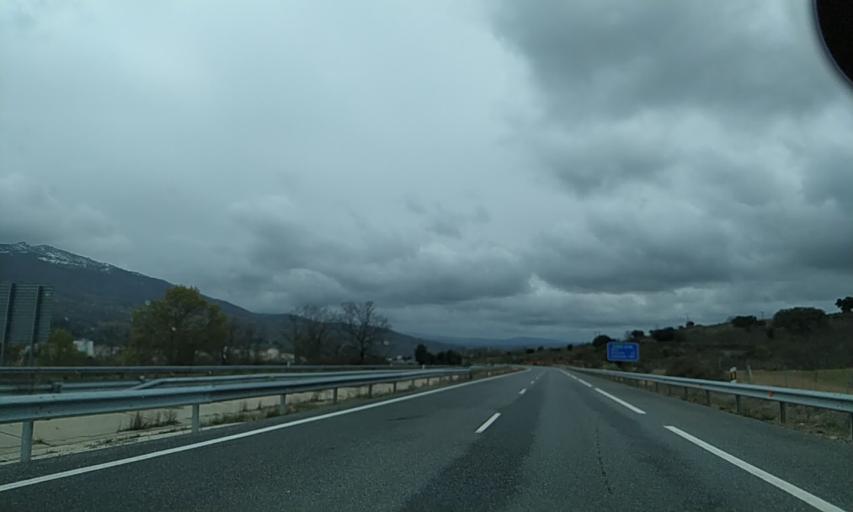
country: ES
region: Castille and Leon
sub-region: Provincia de Salamanca
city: Bejar
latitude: 40.3956
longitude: -5.7549
